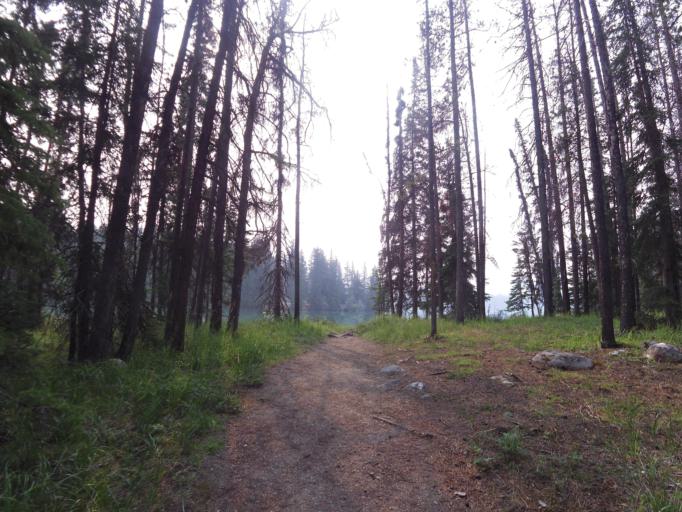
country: CA
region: Alberta
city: Jasper Park Lodge
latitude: 52.8849
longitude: -118.0641
